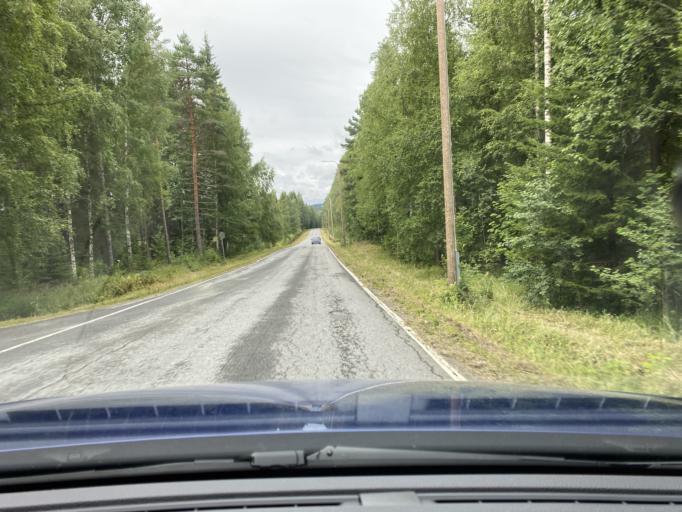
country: FI
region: Pirkanmaa
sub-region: Ylae-Pirkanmaa
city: Maenttae
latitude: 62.0249
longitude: 24.7074
